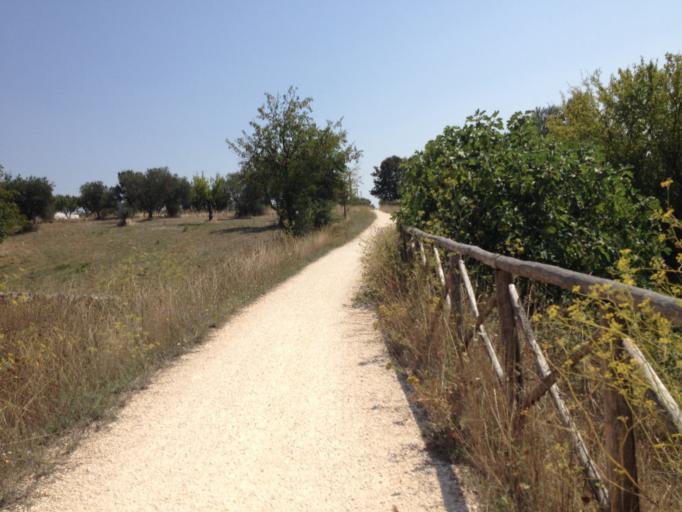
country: IT
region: Apulia
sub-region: Provincia di Brindisi
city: Cisternino
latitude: 40.7166
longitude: 17.4056
